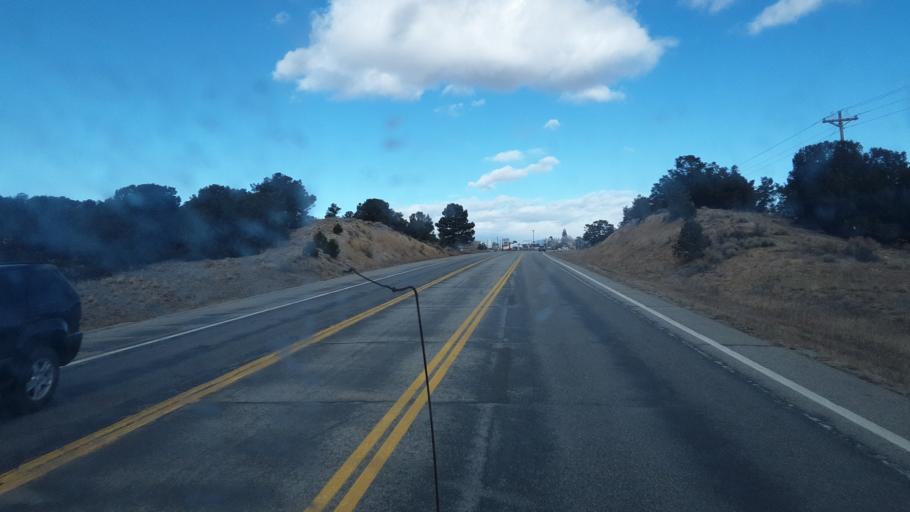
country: US
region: Colorado
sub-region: Chaffee County
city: Salida
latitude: 38.6732
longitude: -106.0914
